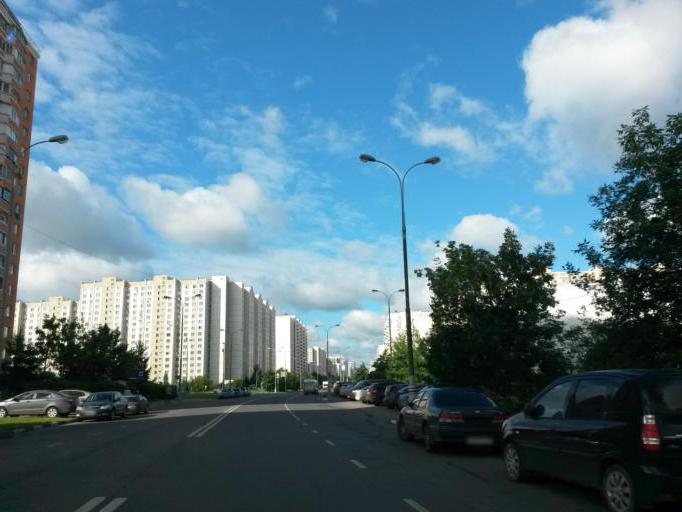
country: RU
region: Moscow
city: Brateyevo
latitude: 55.6596
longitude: 37.7707
